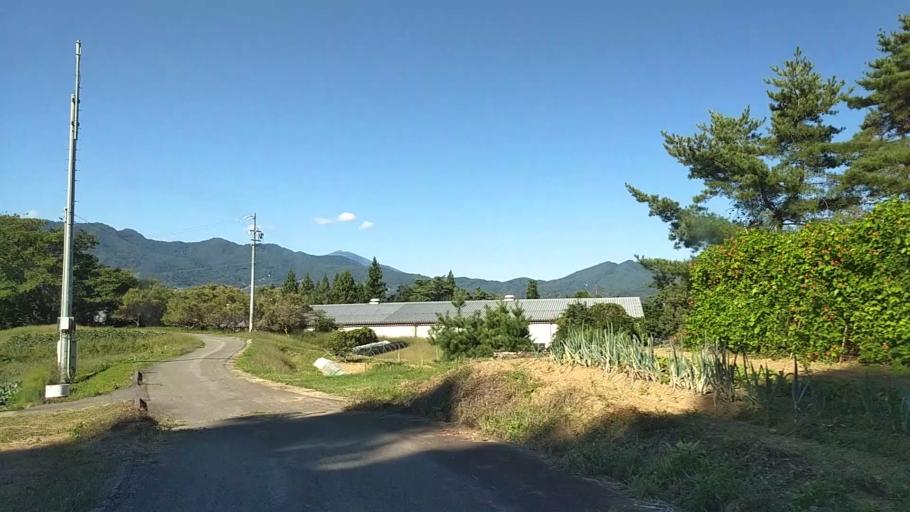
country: JP
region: Nagano
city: Nagano-shi
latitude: 36.5948
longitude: 138.0858
